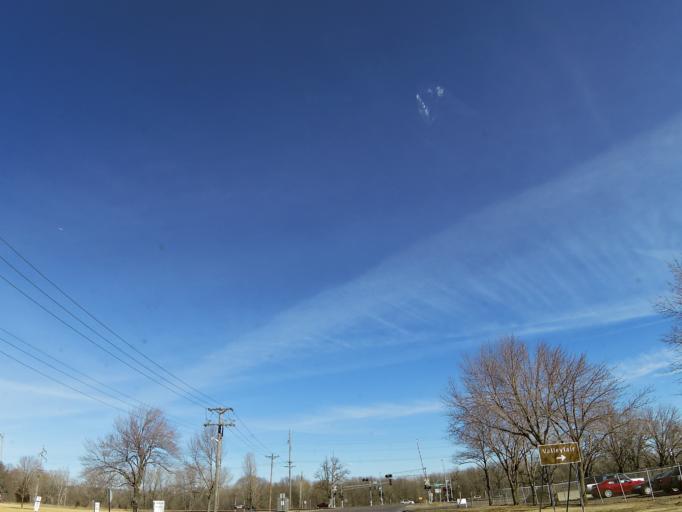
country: US
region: Minnesota
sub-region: Hennepin County
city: Eden Prairie
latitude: 44.7985
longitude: -93.4699
